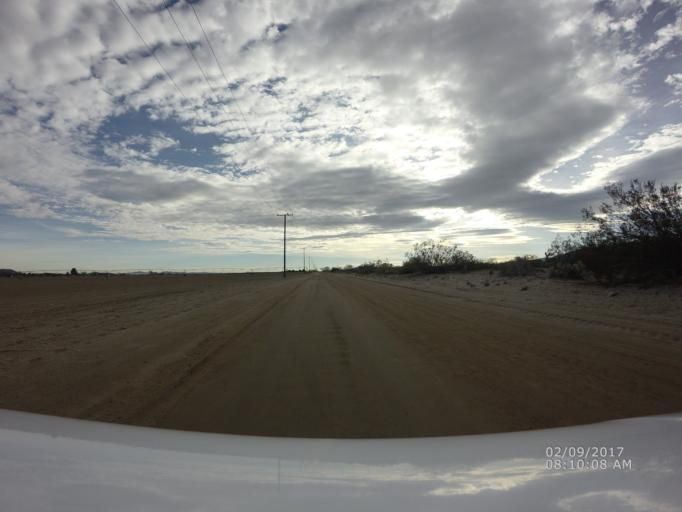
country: US
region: California
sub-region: Los Angeles County
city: Lake Los Angeles
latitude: 34.5725
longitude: -117.8600
